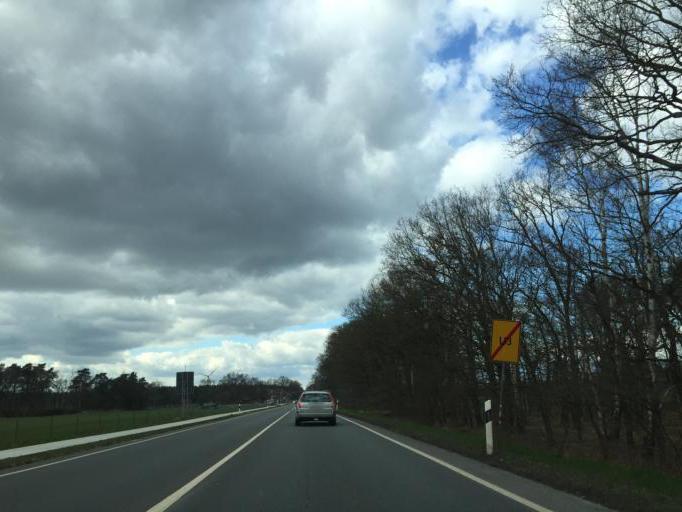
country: DE
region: Lower Saxony
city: Uetze
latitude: 52.4768
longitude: 10.2686
